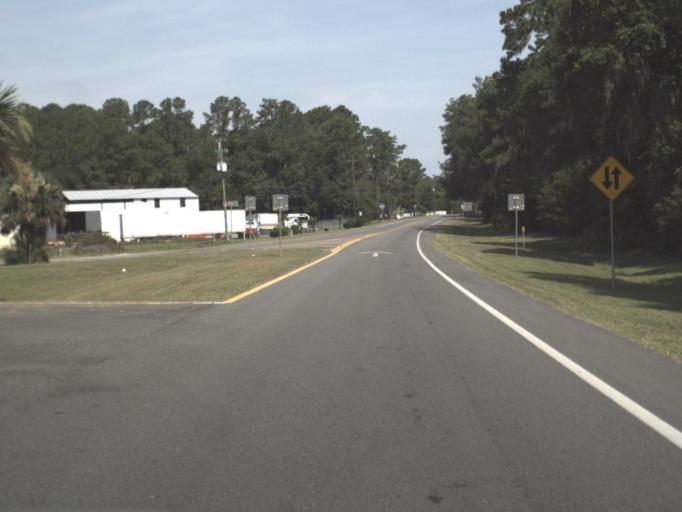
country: US
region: Florida
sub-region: Hamilton County
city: Jasper
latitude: 30.5249
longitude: -82.9622
